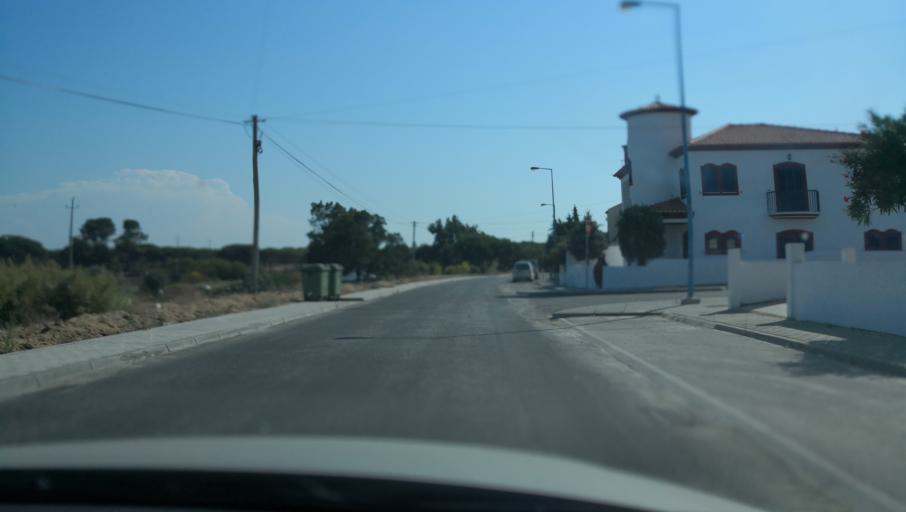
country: PT
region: Setubal
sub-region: Setubal
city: Setubal
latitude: 38.4072
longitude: -8.7522
